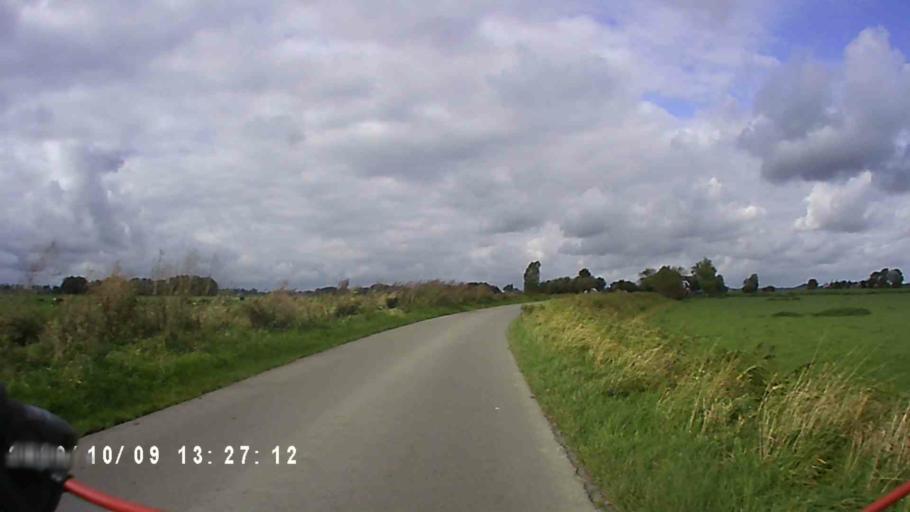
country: NL
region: Groningen
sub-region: Gemeente Zuidhorn
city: Aduard
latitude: 53.2667
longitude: 6.4613
